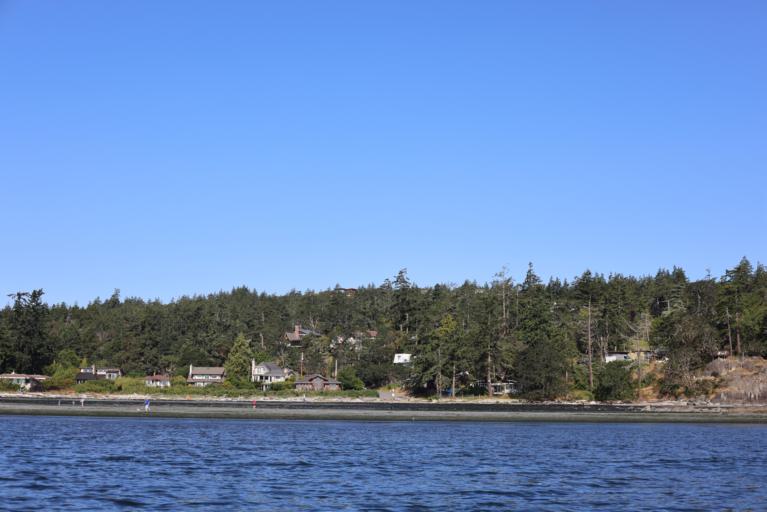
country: CA
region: British Columbia
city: Metchosin
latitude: 48.3544
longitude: -123.5409
